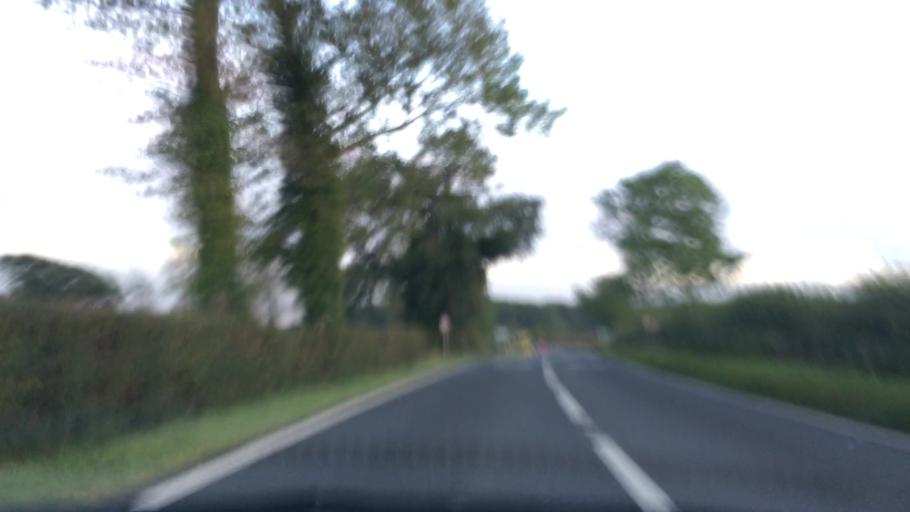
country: GB
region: England
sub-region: North East Lincolnshire
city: Wold Newton
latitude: 53.4581
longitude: -0.0901
